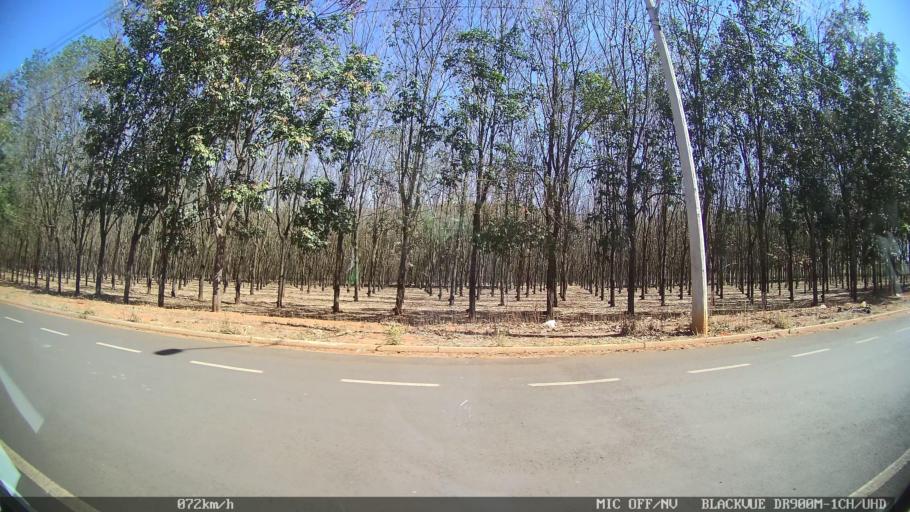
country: BR
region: Sao Paulo
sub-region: Sao Jose Do Rio Preto
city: Sao Jose do Rio Preto
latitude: -20.7357
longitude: -49.4358
